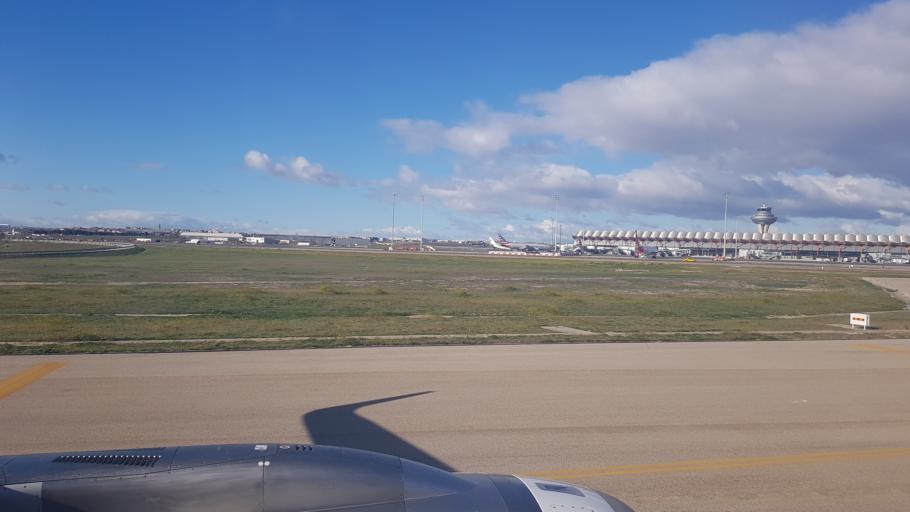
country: ES
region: Madrid
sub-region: Provincia de Madrid
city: Barajas de Madrid
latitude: 40.4922
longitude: -3.5582
